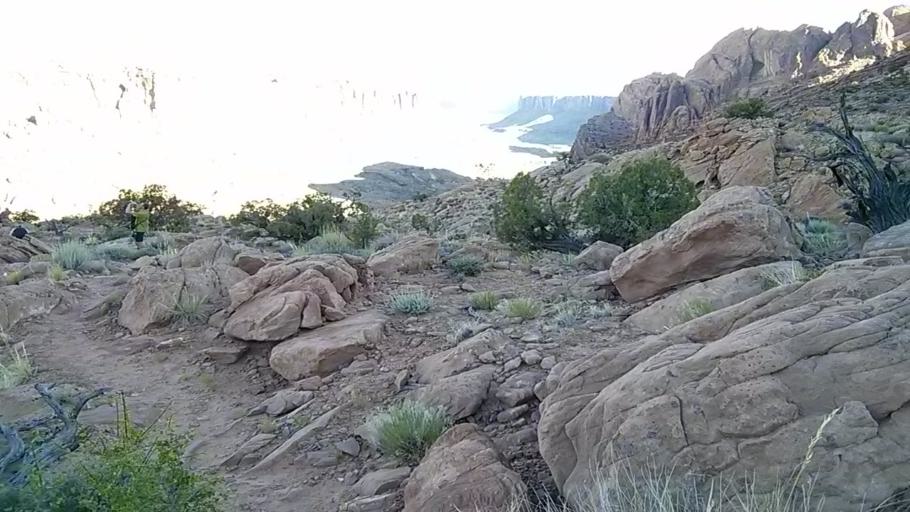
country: US
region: Utah
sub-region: Grand County
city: Moab
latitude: 38.4277
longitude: -109.9429
